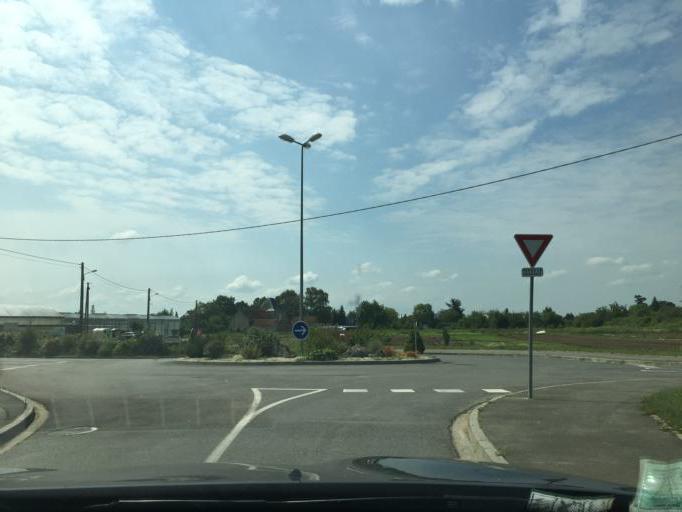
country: FR
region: Centre
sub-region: Departement du Loiret
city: Saint-Denis-en-Val
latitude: 47.8894
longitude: 1.9598
